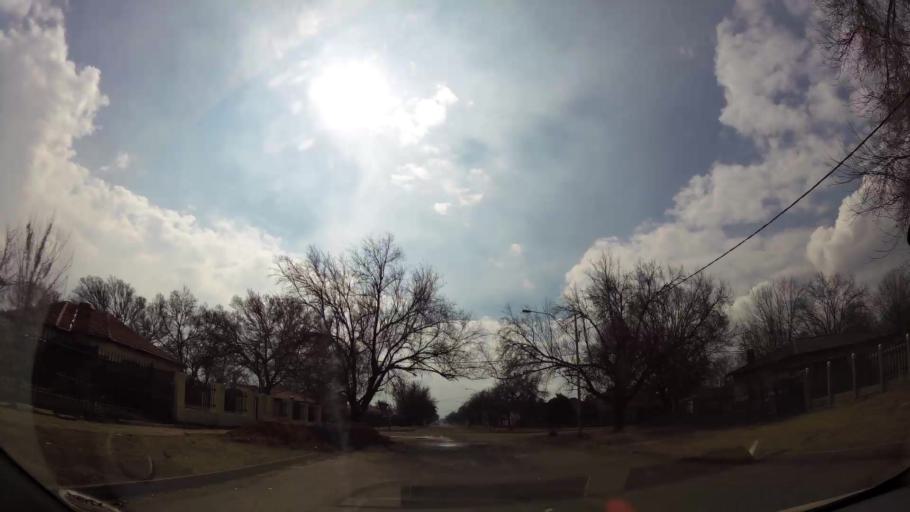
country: ZA
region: Gauteng
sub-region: Sedibeng District Municipality
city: Vereeniging
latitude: -26.6802
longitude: 27.9194
